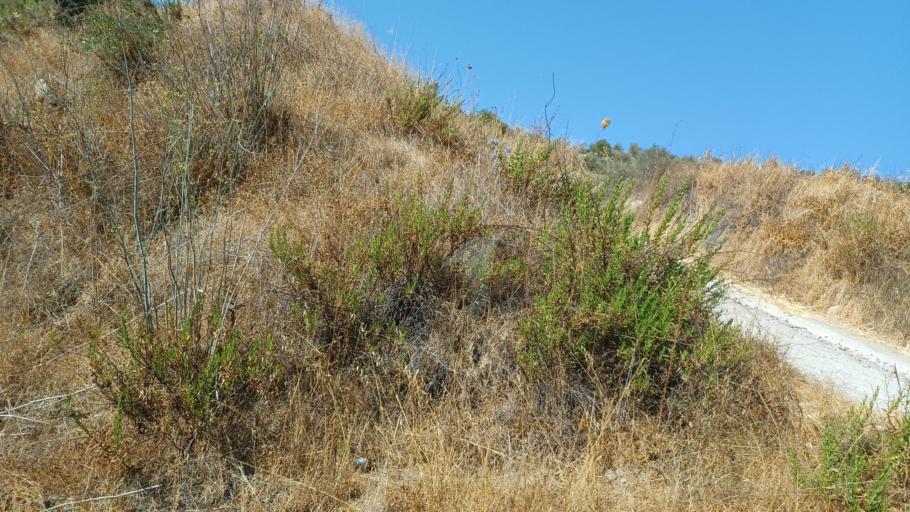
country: CY
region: Pafos
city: Polis
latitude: 34.9445
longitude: 32.5128
